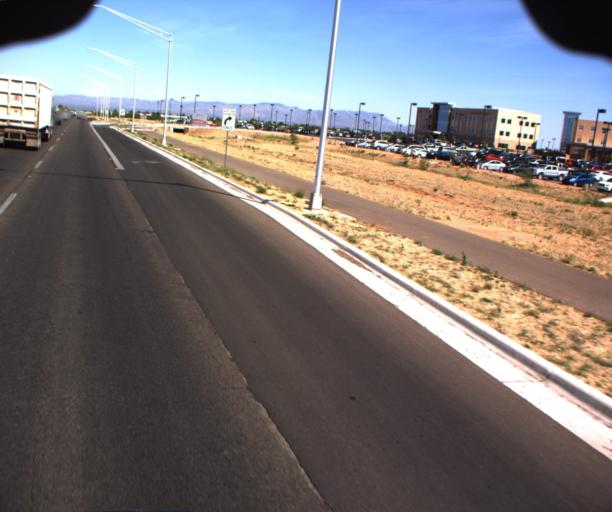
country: US
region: Arizona
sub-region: Cochise County
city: Sierra Vista
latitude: 31.5546
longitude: -110.2314
